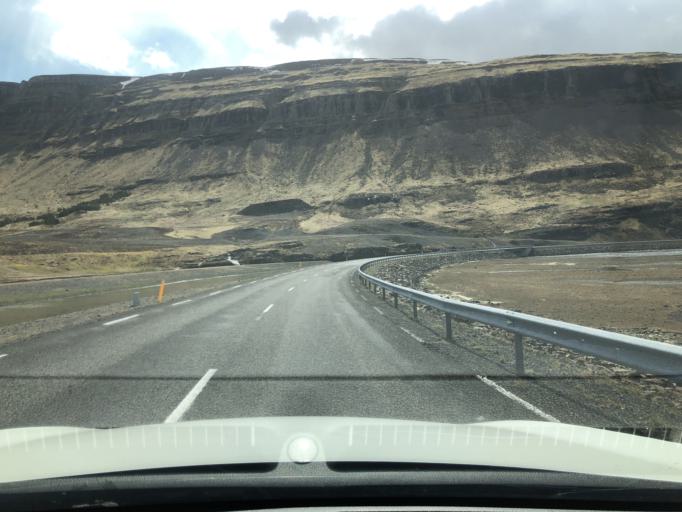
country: IS
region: Capital Region
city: Mosfellsbaer
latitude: 64.3851
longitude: -21.3548
